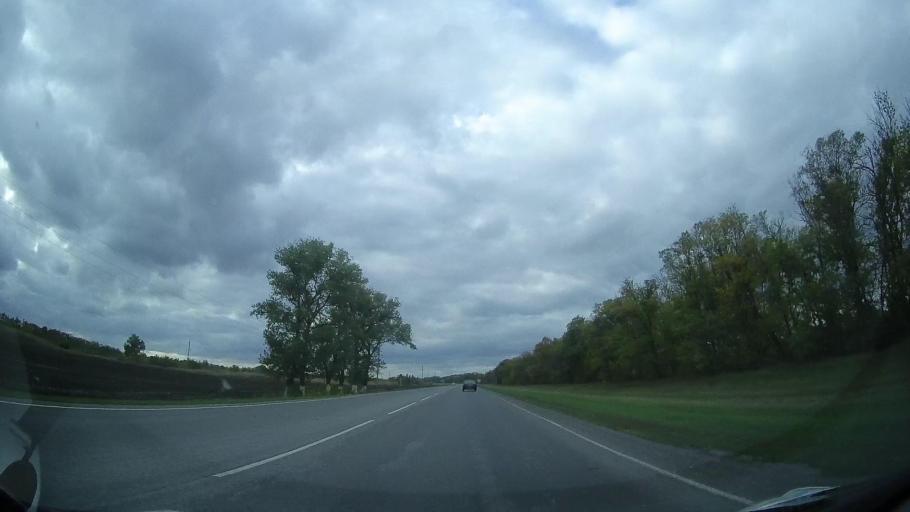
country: RU
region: Rostov
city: Zernograd
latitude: 46.8006
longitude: 40.3609
